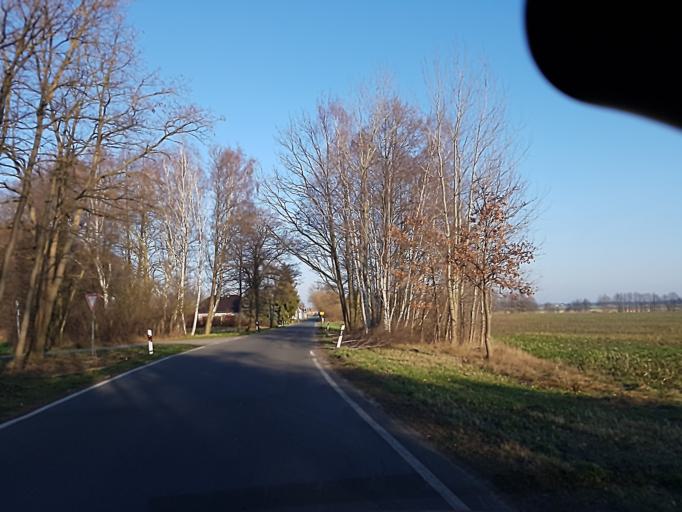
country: DE
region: Brandenburg
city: Schonborn
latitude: 51.5631
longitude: 13.5209
